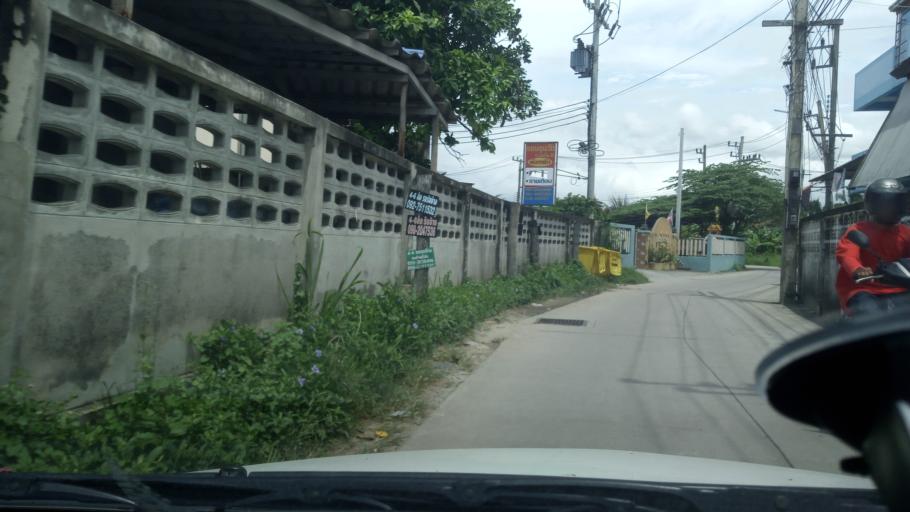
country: TH
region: Chon Buri
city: Phan Thong
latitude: 13.4149
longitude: 101.0503
